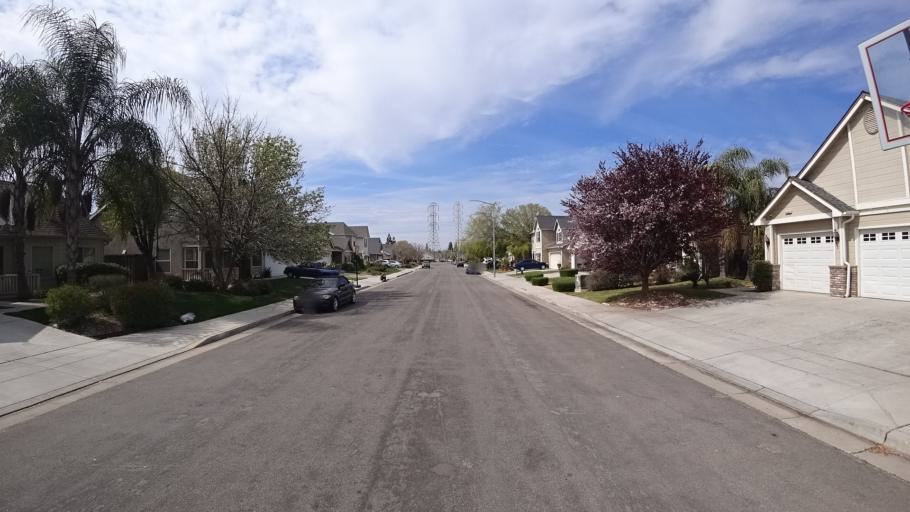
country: US
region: California
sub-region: Fresno County
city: West Park
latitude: 36.8208
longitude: -119.8772
